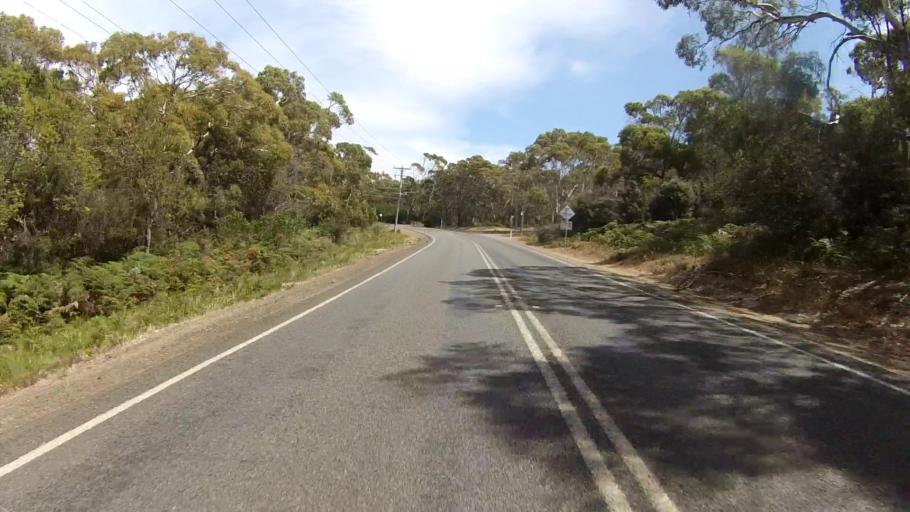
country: AU
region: Tasmania
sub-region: Clarence
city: Sandford
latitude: -43.0245
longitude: 147.4846
